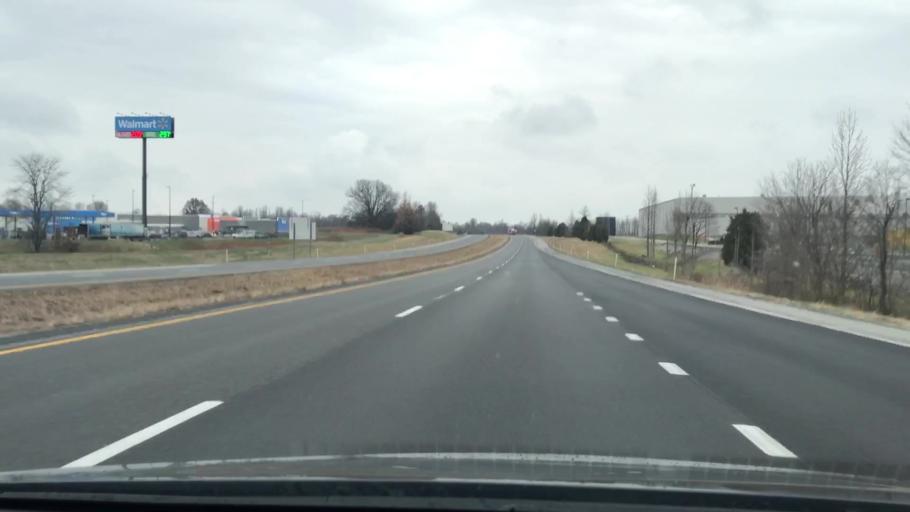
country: US
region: Kentucky
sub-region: Hopkins County
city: Madisonville
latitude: 37.4201
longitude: -87.4721
